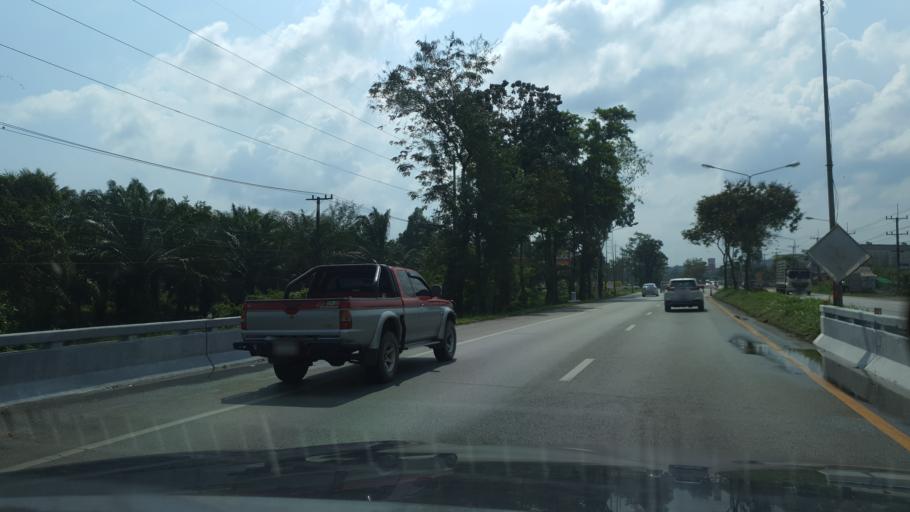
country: TH
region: Chumphon
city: Chumphon
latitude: 10.5660
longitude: 99.1156
